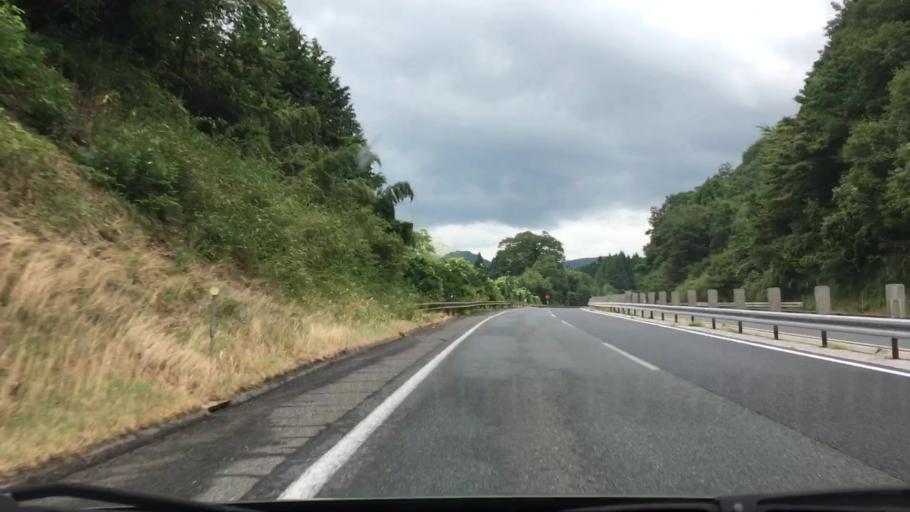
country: JP
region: Okayama
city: Niimi
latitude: 34.9344
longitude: 133.3281
